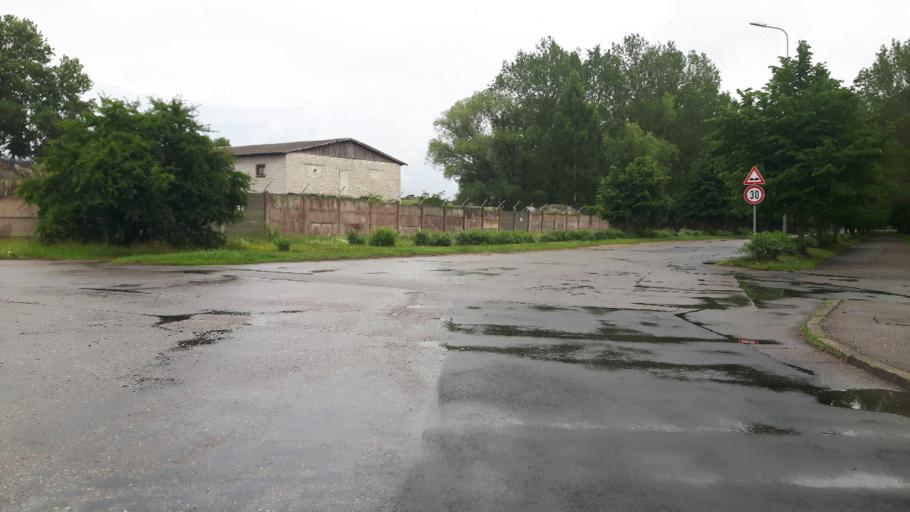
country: LV
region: Liepaja
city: Liepaja
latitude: 56.5142
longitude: 20.9909
